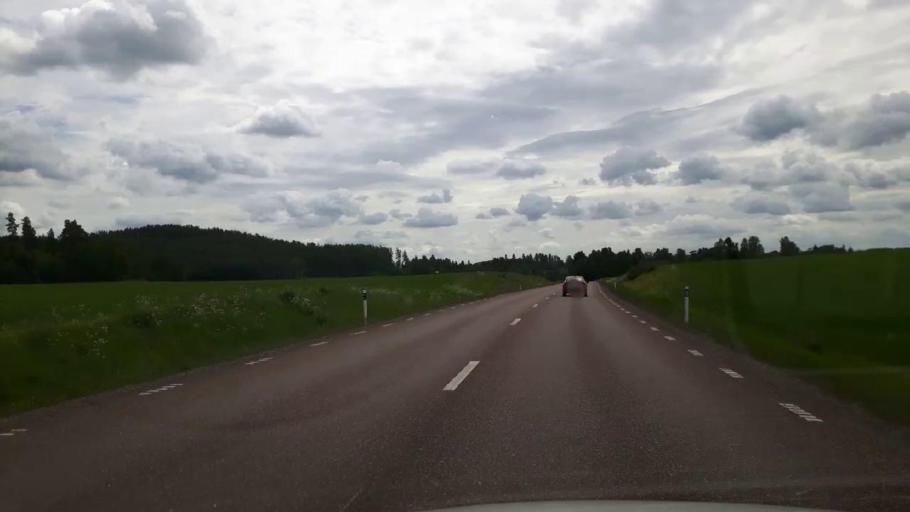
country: SE
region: Dalarna
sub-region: Hedemora Kommun
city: Hedemora
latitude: 60.3294
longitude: 15.9496
